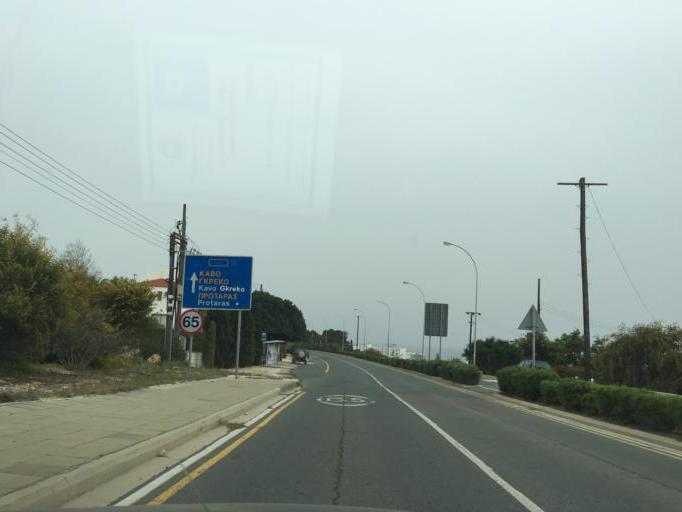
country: CY
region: Ammochostos
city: Ayia Napa
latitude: 34.9926
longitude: 34.0024
